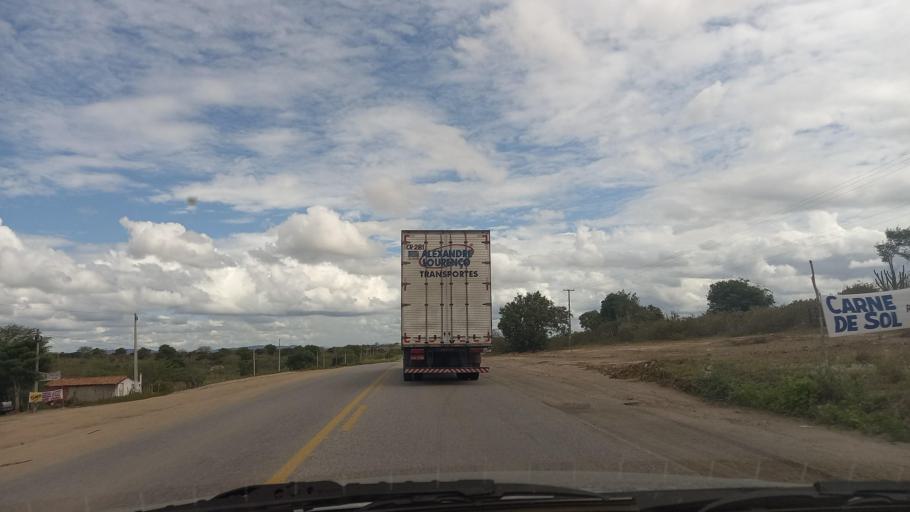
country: BR
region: Pernambuco
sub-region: Cachoeirinha
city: Cachoeirinha
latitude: -8.3895
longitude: -36.1775
